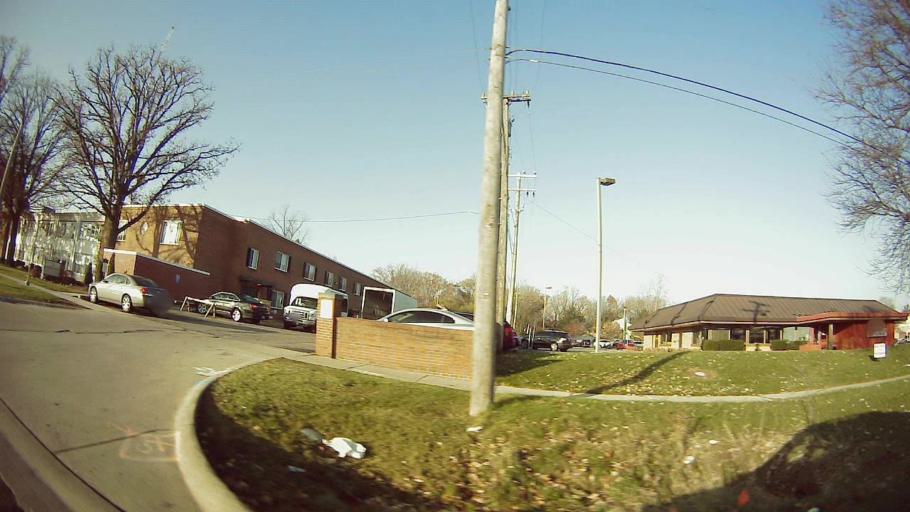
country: US
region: Michigan
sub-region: Oakland County
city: Lathrup Village
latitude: 42.4862
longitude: -83.2024
